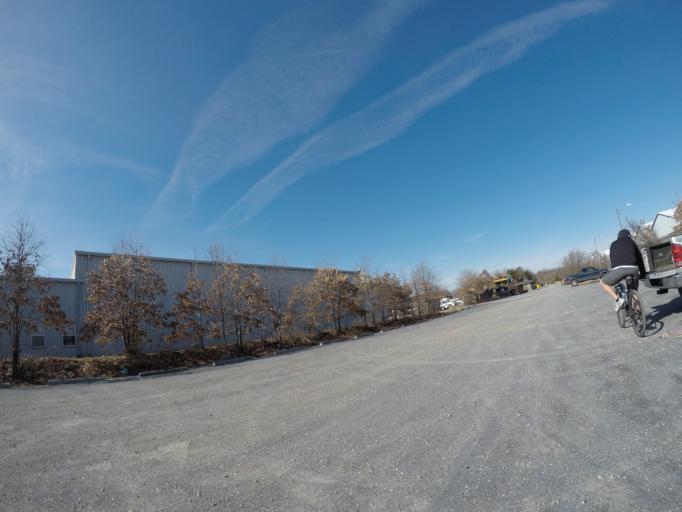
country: US
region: Maryland
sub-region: Charles County
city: Saint Charles
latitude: 38.5896
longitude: -76.9453
